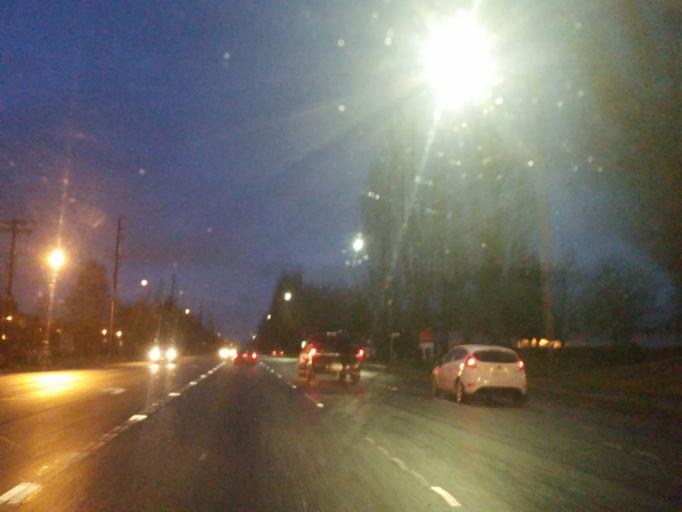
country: US
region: Washington
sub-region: King County
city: Kent
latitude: 47.4094
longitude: -122.2495
